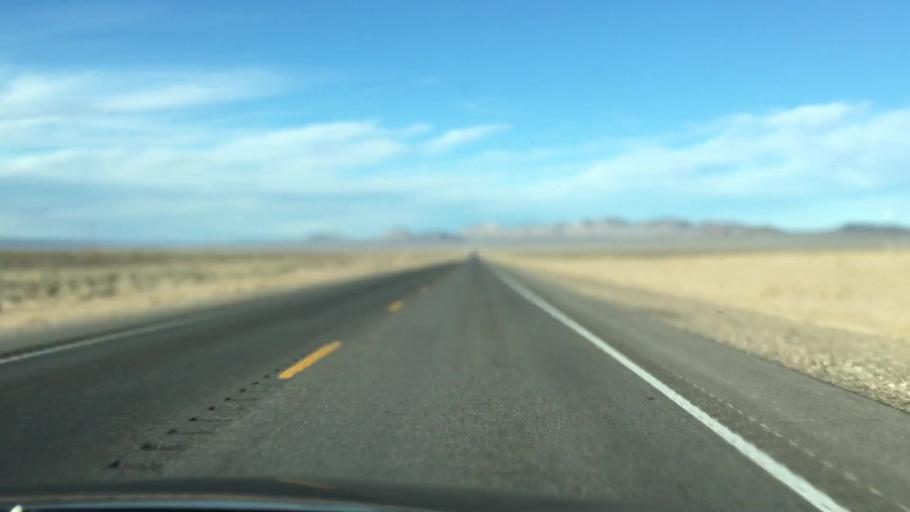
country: US
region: Nevada
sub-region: Esmeralda County
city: Goldfield
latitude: 37.8078
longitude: -117.2396
